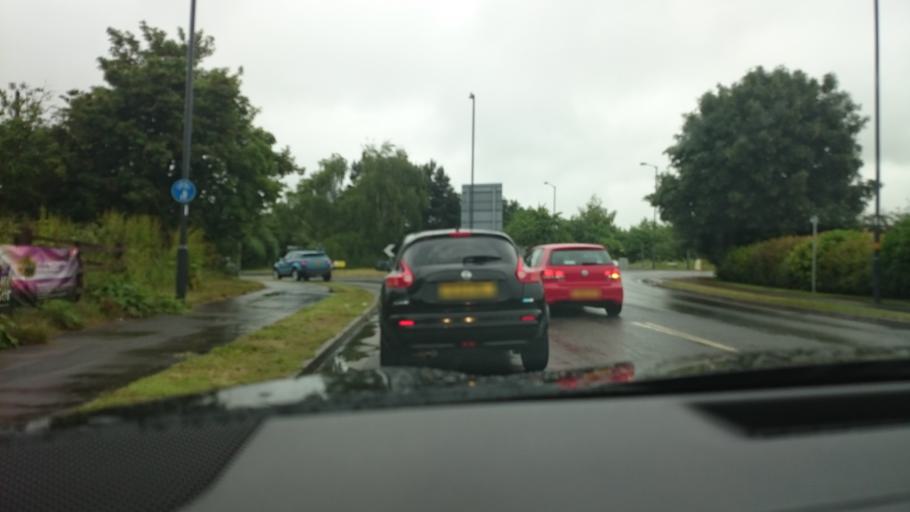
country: GB
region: England
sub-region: Warwickshire
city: Stratford-upon-Avon
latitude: 52.1805
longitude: -1.7006
